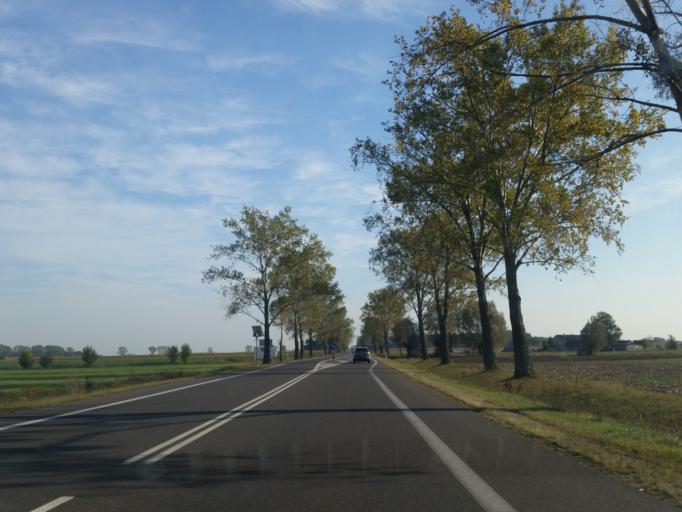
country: PL
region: Masovian Voivodeship
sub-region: Powiat plocki
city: Drobin
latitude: 52.7145
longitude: 20.0240
